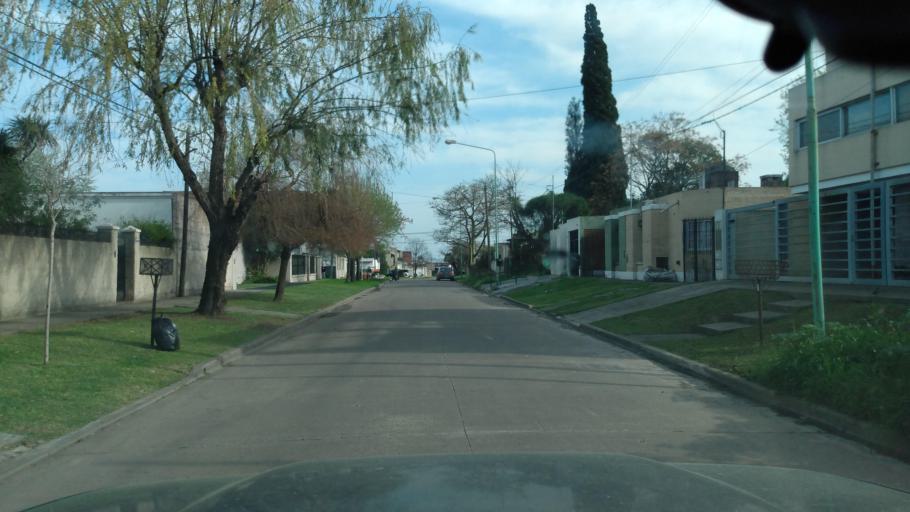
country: AR
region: Buenos Aires
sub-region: Partido de Lujan
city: Lujan
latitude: -34.5769
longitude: -59.1122
